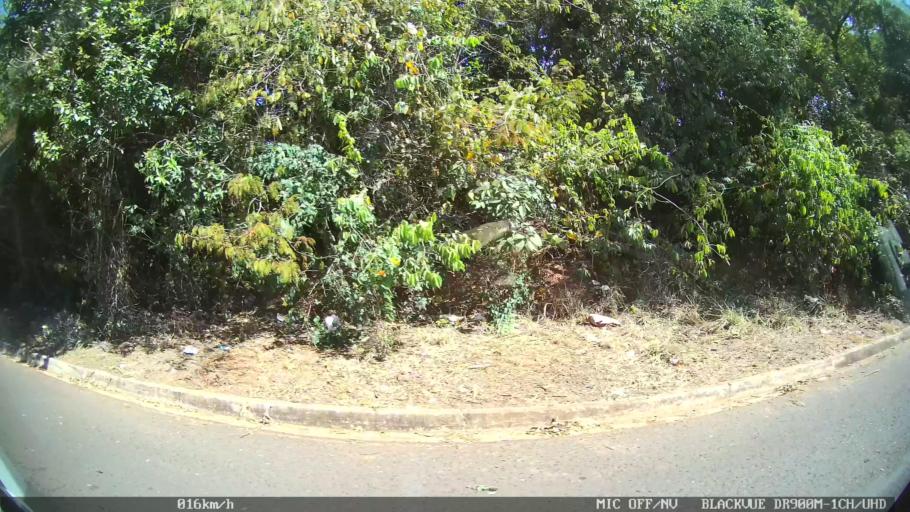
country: BR
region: Sao Paulo
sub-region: Franca
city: Franca
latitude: -20.5391
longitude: -47.4613
